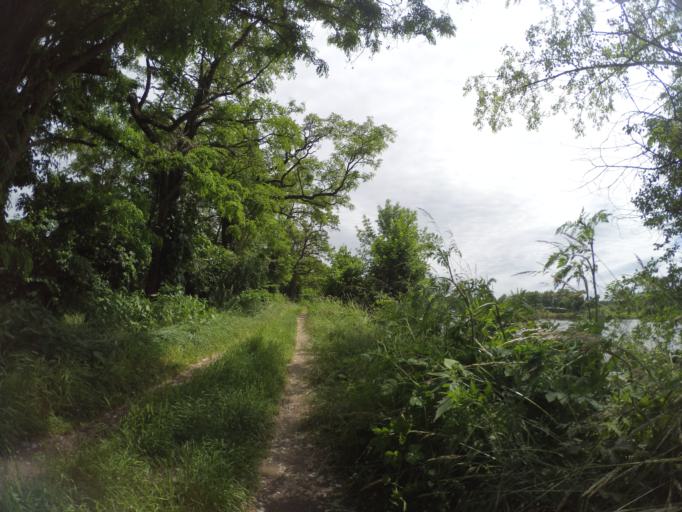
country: CZ
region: Central Bohemia
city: Lysa nad Labem
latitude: 50.1799
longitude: 14.8523
